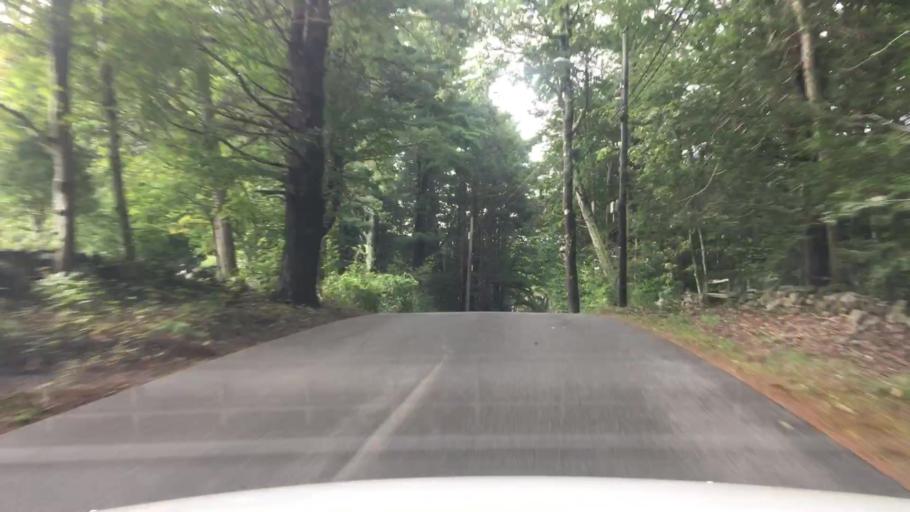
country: US
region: Maine
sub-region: York County
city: Kittery Point
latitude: 43.1147
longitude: -70.6836
